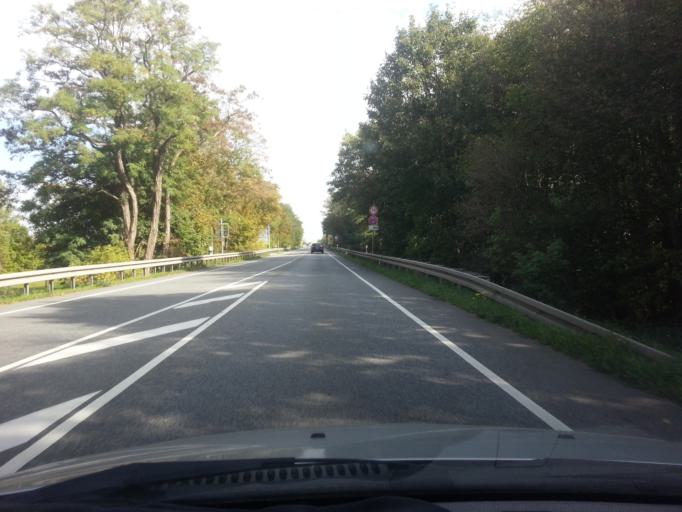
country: DE
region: Hesse
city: Kelsterbach
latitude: 50.0502
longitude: 8.5064
